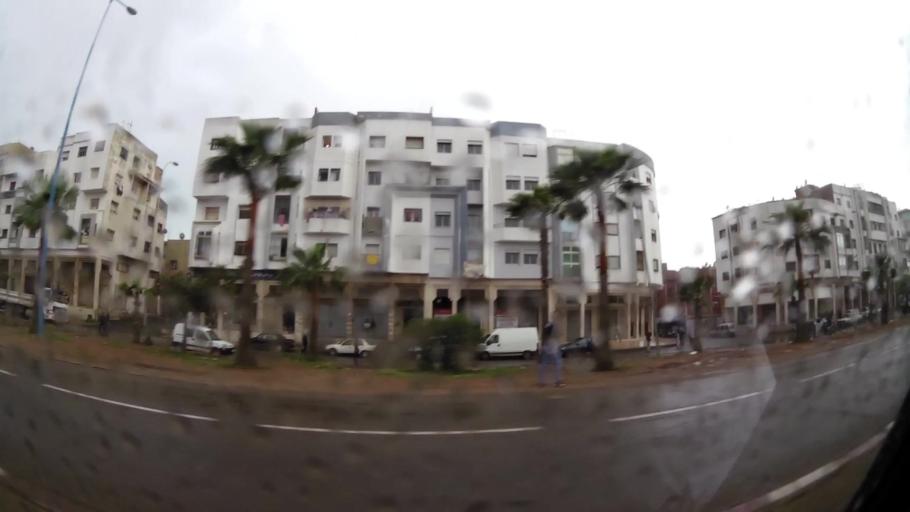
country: MA
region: Grand Casablanca
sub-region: Mediouna
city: Tit Mellil
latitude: 33.5718
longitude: -7.5288
